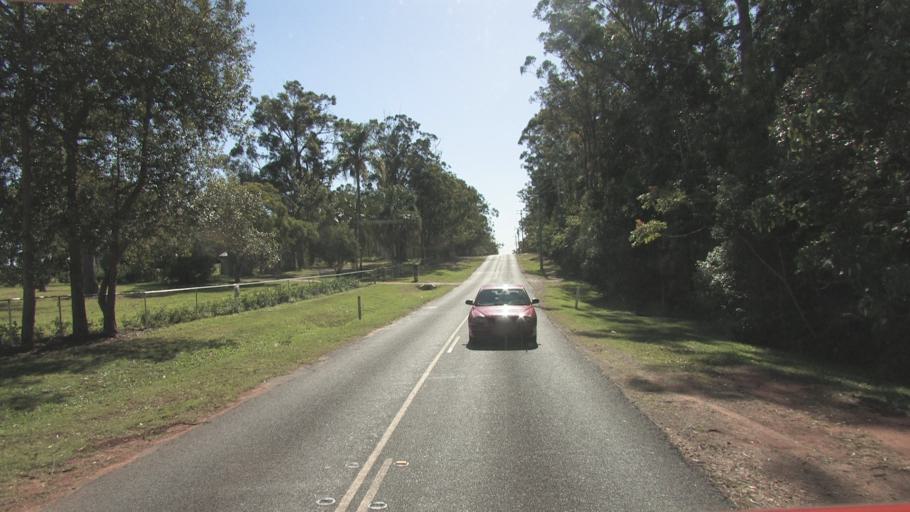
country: AU
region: Queensland
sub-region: Logan
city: Springwood
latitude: -27.5936
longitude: 153.1577
